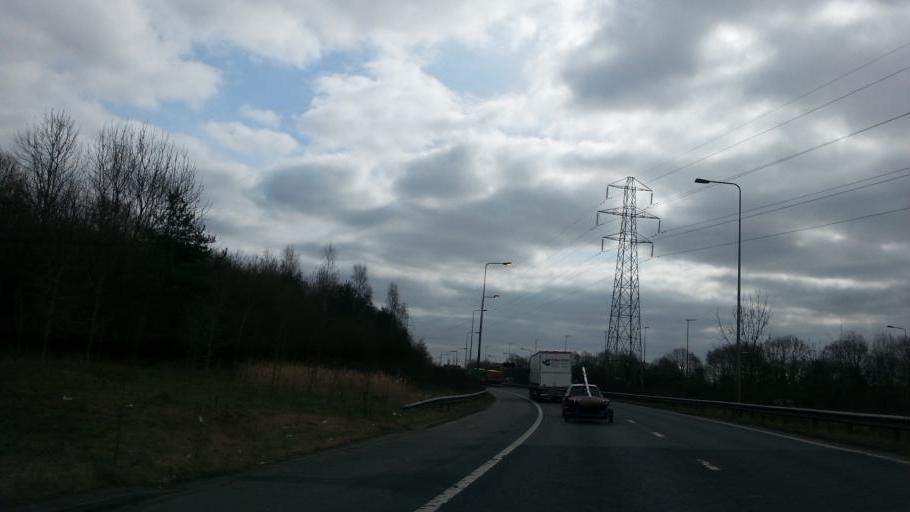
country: GB
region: England
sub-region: Warrington
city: Croft
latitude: 53.4223
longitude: -2.5483
